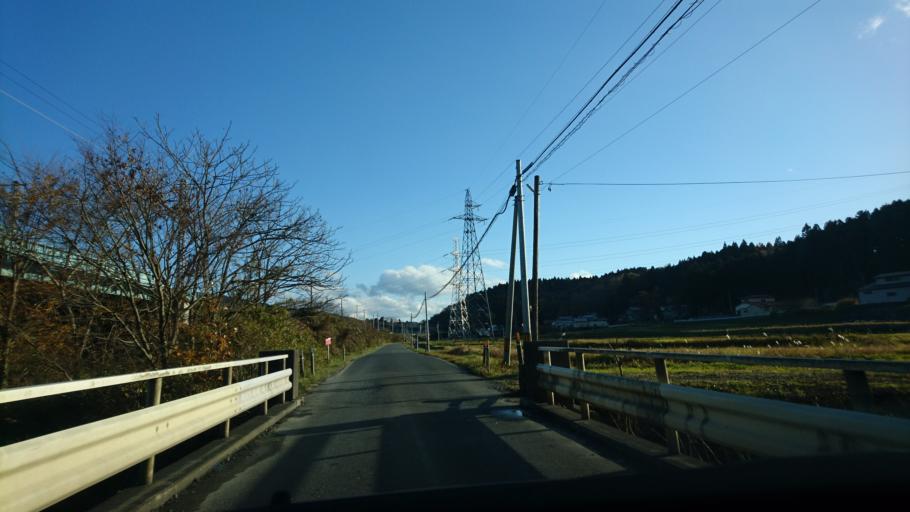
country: JP
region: Iwate
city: Mizusawa
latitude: 39.0284
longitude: 141.1281
